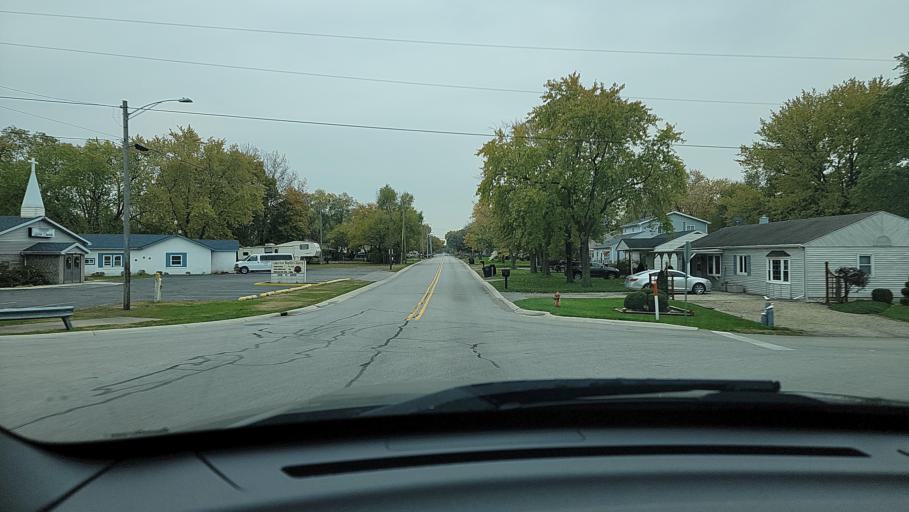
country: US
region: Indiana
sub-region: Lake County
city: Lake Station
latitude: 41.5854
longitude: -87.2124
